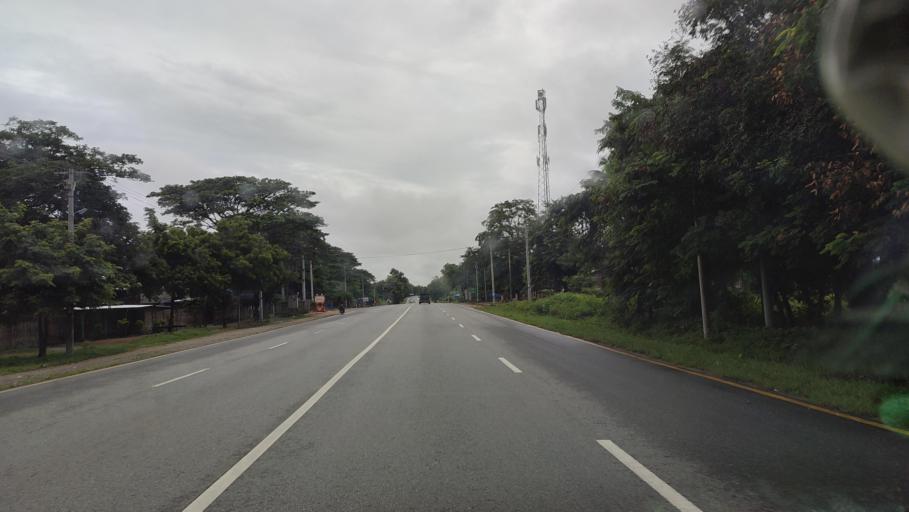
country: MM
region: Mandalay
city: Pyinmana
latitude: 19.9878
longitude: 96.2489
